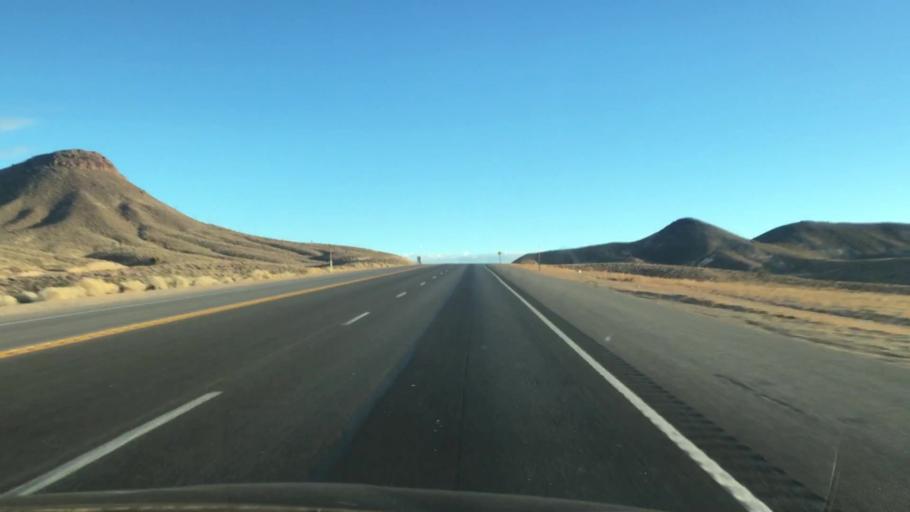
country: US
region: Nevada
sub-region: Esmeralda County
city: Goldfield
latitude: 37.6852
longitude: -117.2315
